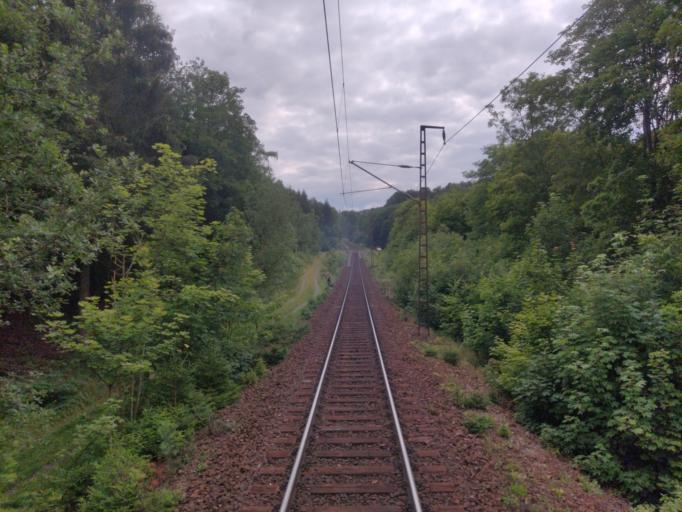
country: DE
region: Saxony-Anhalt
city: Huttenrode
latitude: 51.7791
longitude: 10.9097
